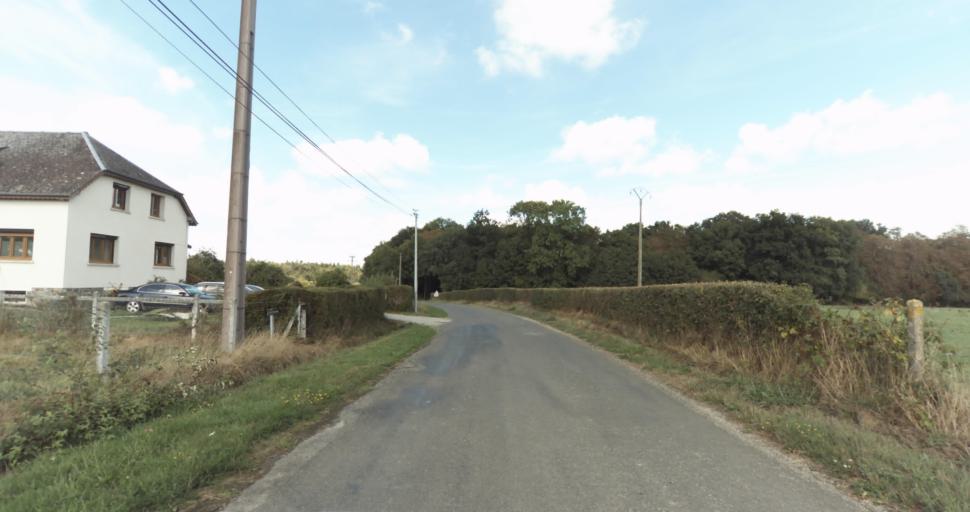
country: FR
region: Lower Normandy
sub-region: Departement du Calvados
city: Orbec
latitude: 48.9451
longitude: 0.3757
